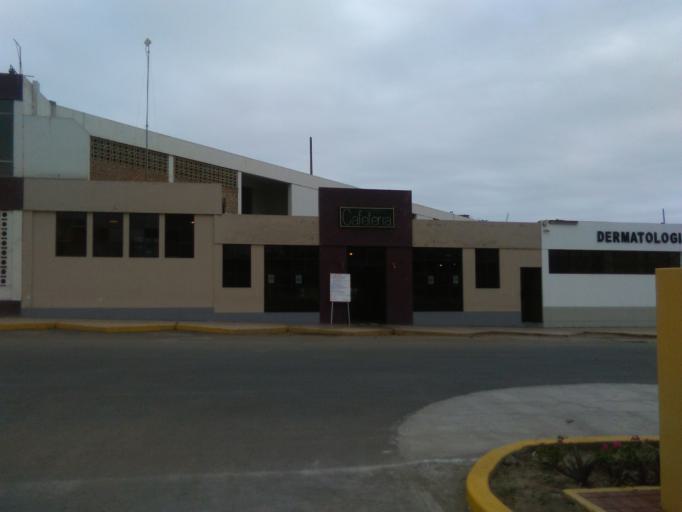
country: PE
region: Callao
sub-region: Callao
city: Callao
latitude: -12.0557
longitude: -77.0817
